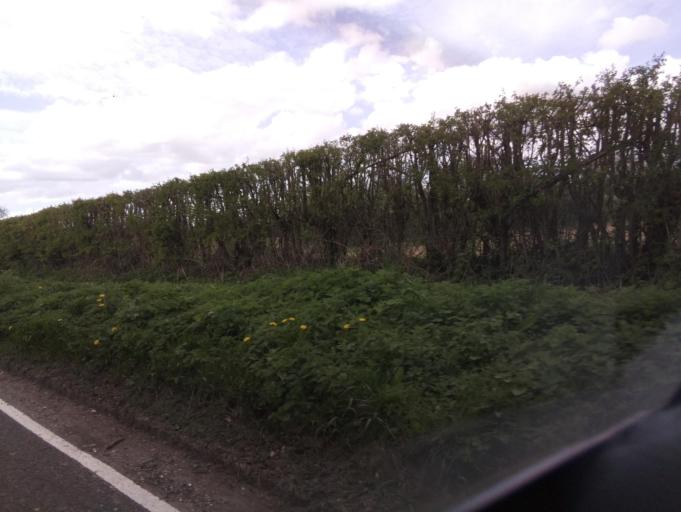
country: GB
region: England
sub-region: Hampshire
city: Chandlers Ford
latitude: 51.0207
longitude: -1.3879
